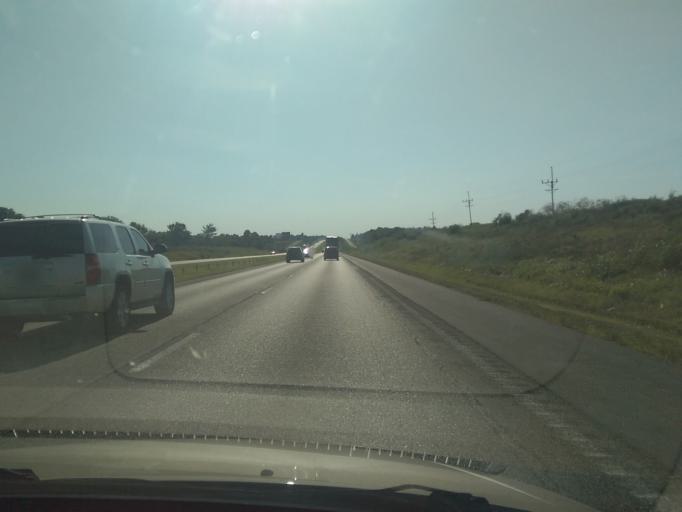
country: US
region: Missouri
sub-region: Lafayette County
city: Higginsville
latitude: 39.0020
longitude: -93.7798
